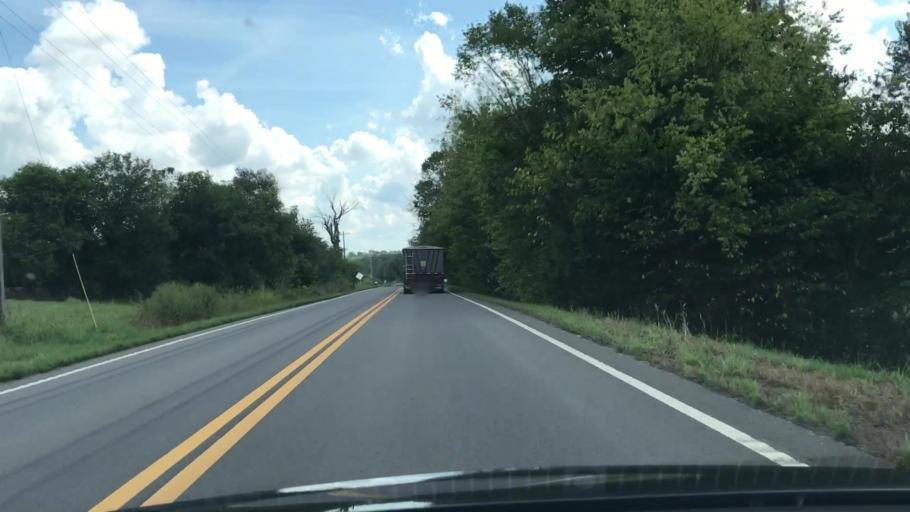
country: US
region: Tennessee
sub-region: Robertson County
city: Springfield
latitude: 36.6339
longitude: -86.9698
